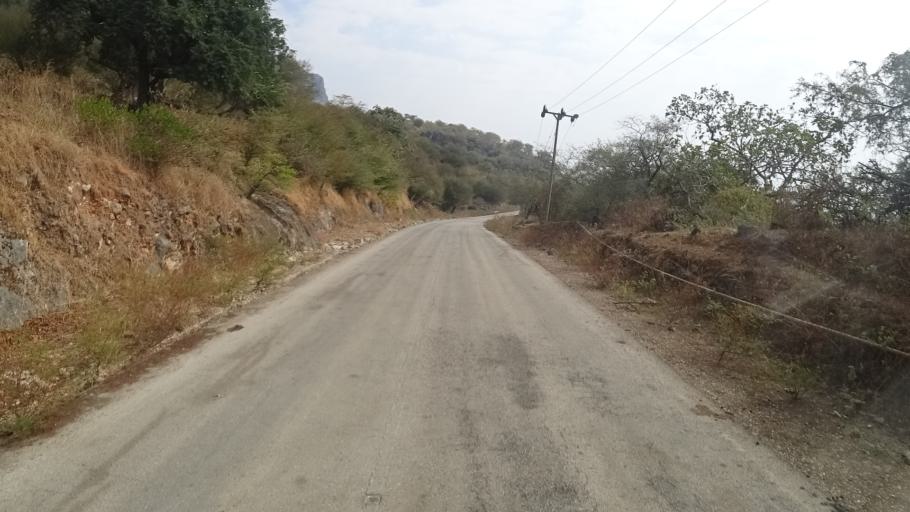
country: YE
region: Al Mahrah
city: Hawf
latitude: 16.7073
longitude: 53.2198
